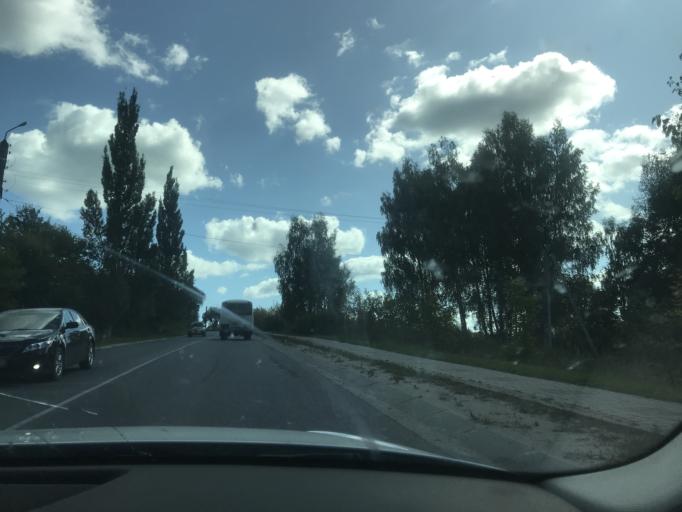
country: RU
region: Kaluga
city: Kondrovo
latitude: 54.8073
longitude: 35.9340
